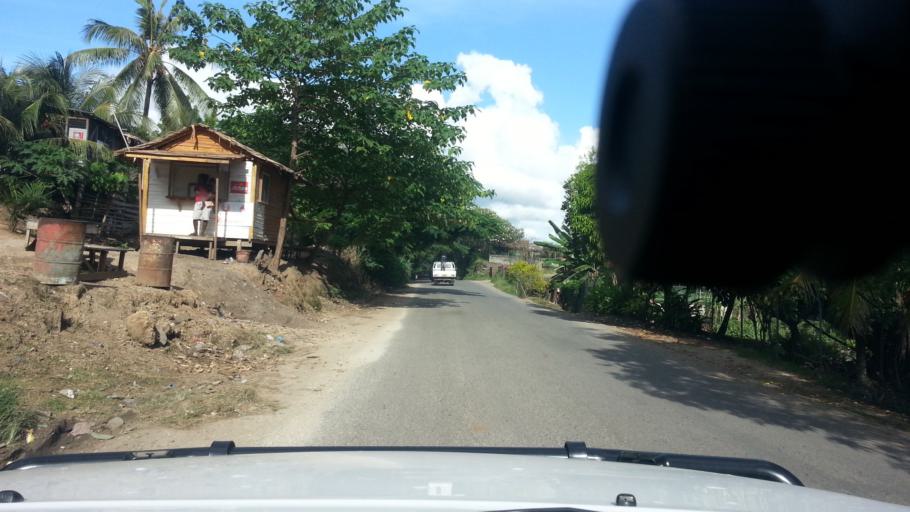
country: SB
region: Guadalcanal
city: Honiara
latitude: -9.4424
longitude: 159.9776
